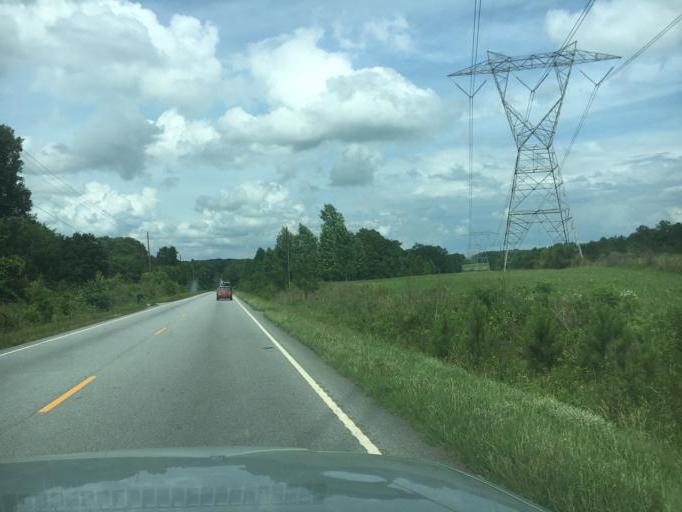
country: US
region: South Carolina
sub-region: Greenville County
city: Simpsonville
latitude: 34.6501
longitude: -82.3046
